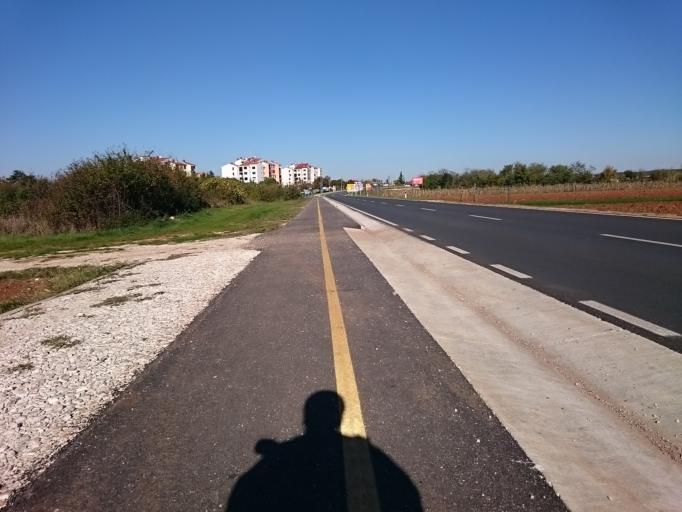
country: HR
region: Istarska
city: Umag
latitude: 45.4266
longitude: 13.5303
